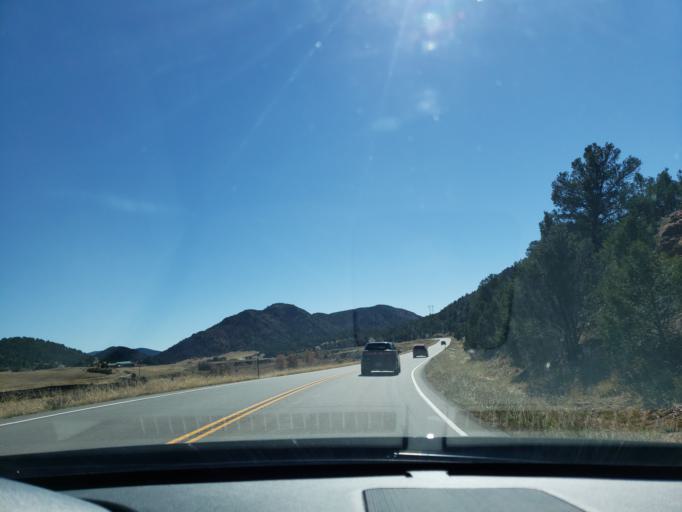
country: US
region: Colorado
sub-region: Fremont County
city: Canon City
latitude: 38.5949
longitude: -105.4252
